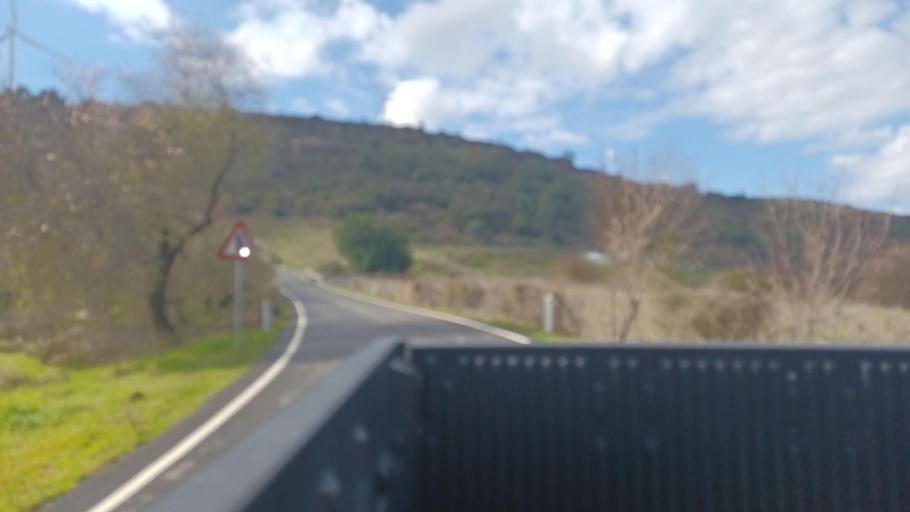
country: CY
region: Limassol
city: Pissouri
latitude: 34.7473
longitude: 32.6658
